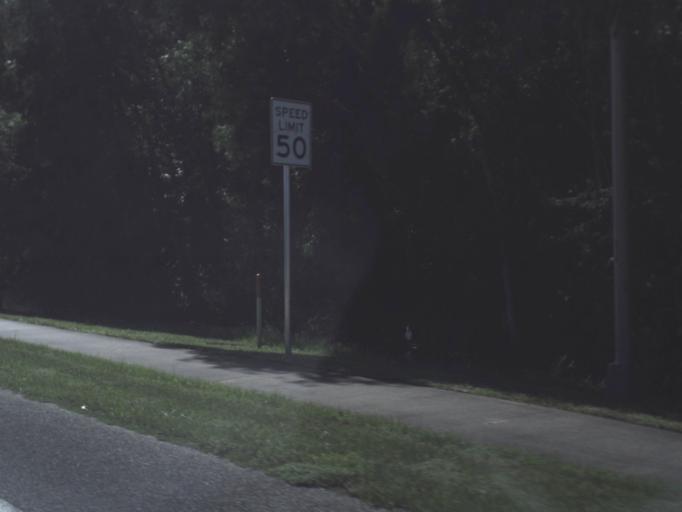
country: US
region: Florida
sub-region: Collier County
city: Lely Resort
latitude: 26.0729
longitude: -81.7144
